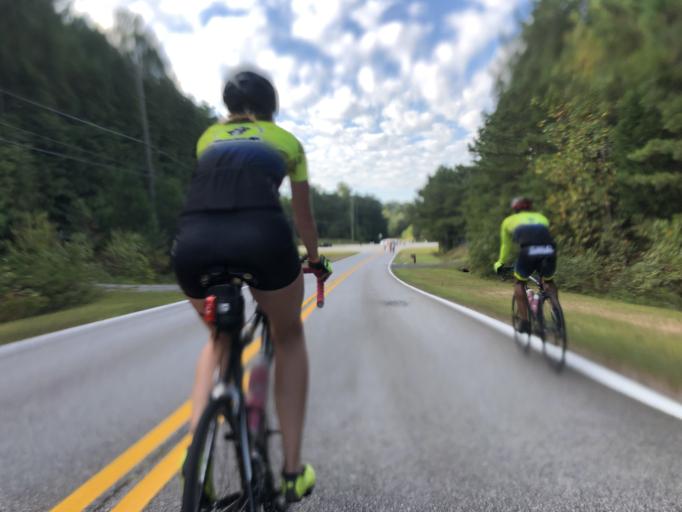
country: US
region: Georgia
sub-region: Fulton County
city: Palmetto
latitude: 33.5867
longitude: -84.6518
